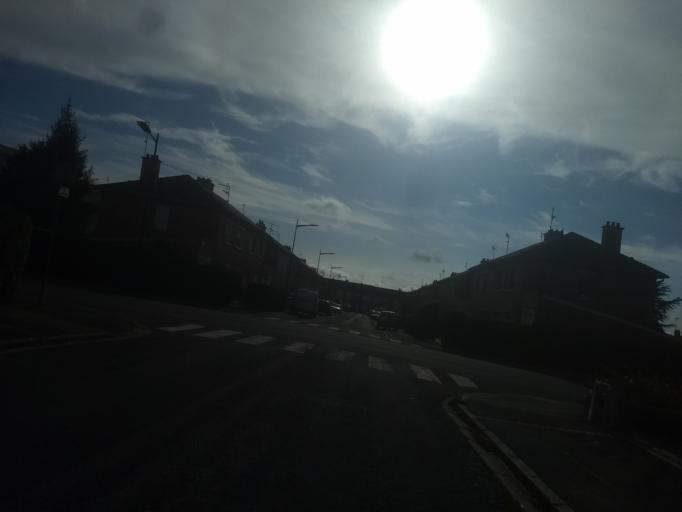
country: FR
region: Nord-Pas-de-Calais
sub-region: Departement du Pas-de-Calais
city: Achicourt
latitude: 50.2907
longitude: 2.7464
